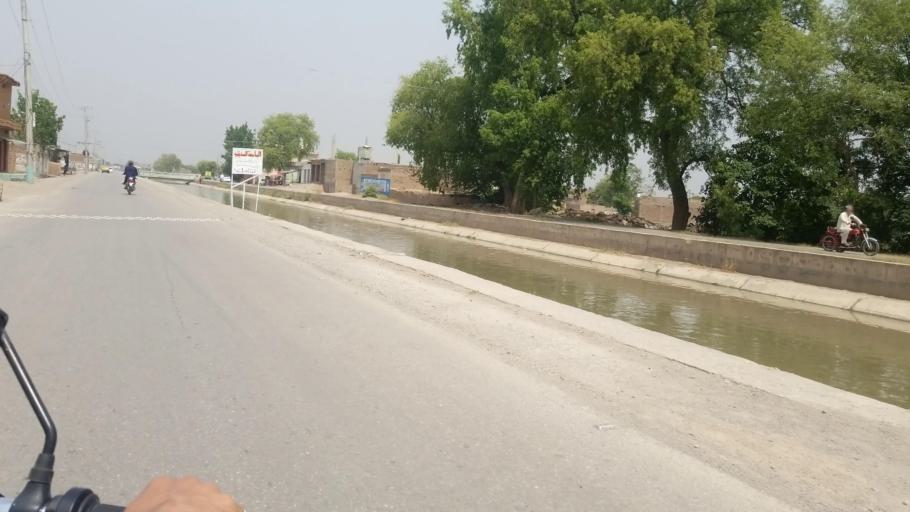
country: PK
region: Khyber Pakhtunkhwa
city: Peshawar
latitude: 33.9508
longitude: 71.5528
